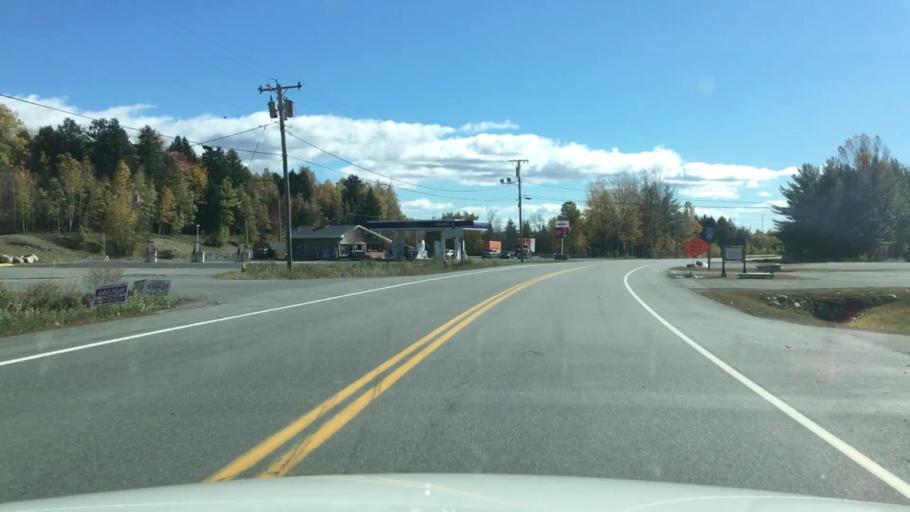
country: US
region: Maine
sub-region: Penobscot County
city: Medway
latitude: 45.6104
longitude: -68.5250
